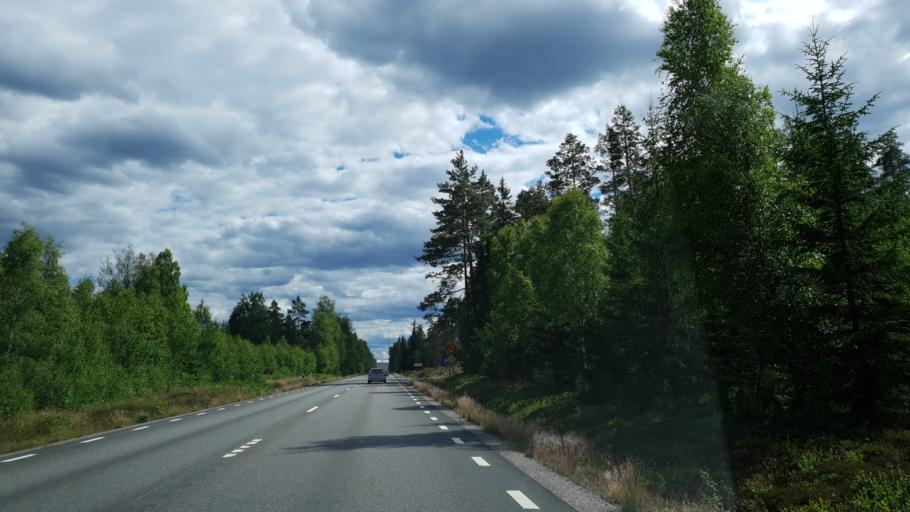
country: SE
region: Kronoberg
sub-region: Lessebo Kommun
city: Lessebo
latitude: 56.7901
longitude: 15.4136
